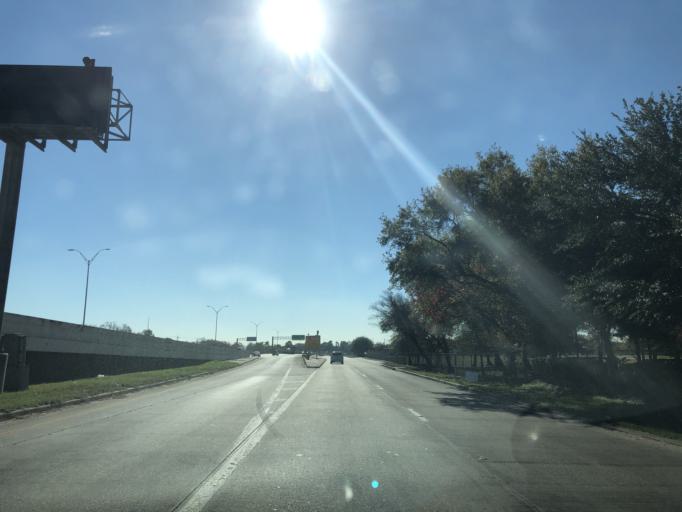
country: US
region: Texas
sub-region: Harris County
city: Cloverleaf
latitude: 29.7881
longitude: -95.1606
